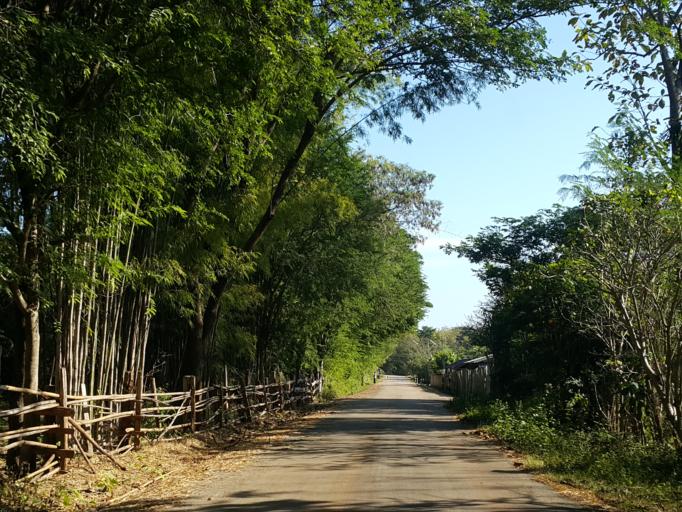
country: TH
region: Lampang
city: Mae Mo
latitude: 18.2988
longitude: 99.6633
